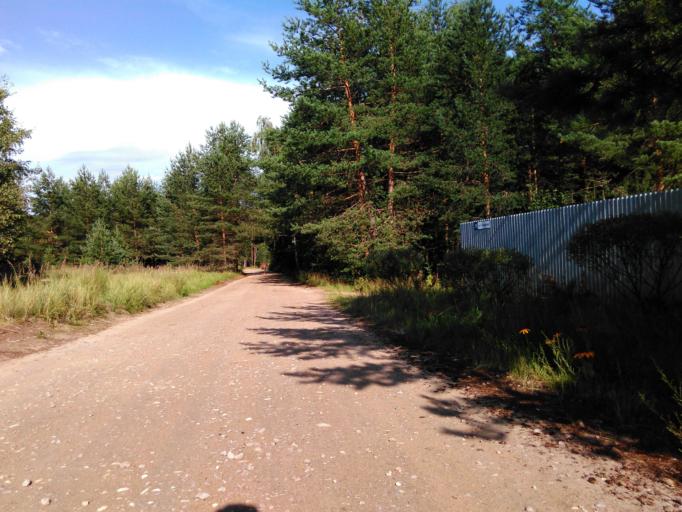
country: RU
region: Vladimir
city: Pokrov
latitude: 55.9705
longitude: 39.1066
